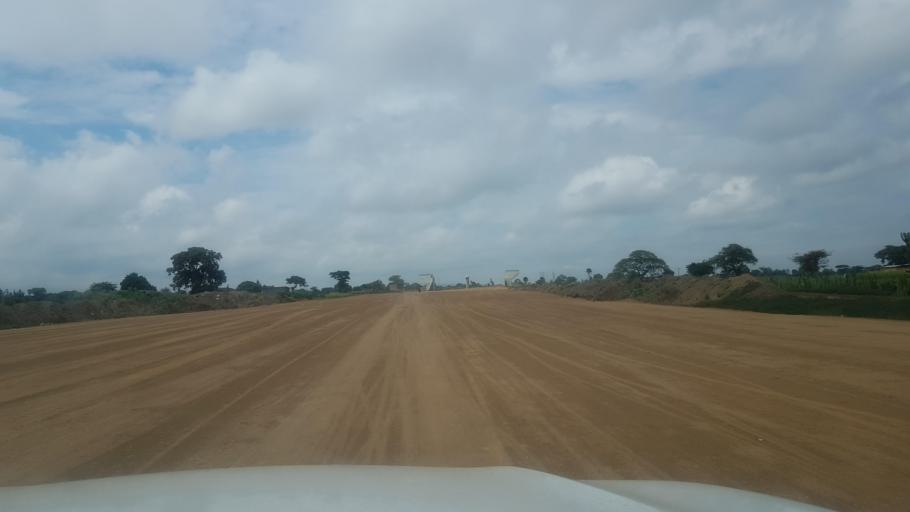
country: ET
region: Oromiya
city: Shashemene
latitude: 7.2594
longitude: 38.5952
